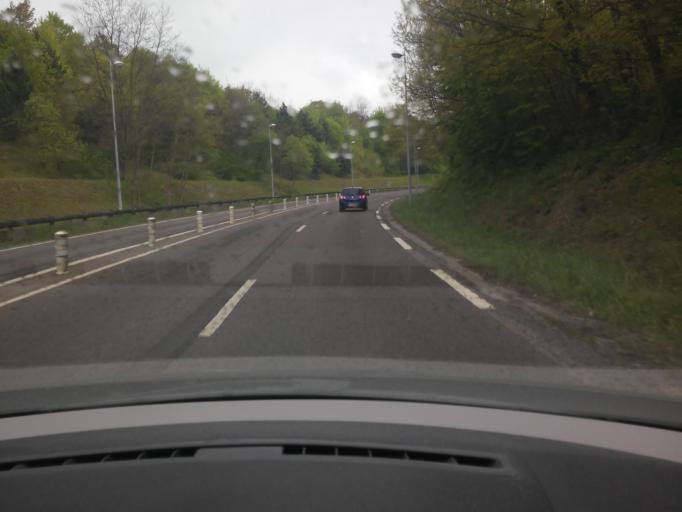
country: FR
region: Lorraine
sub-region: Departement de Meurthe-et-Moselle
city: Laxou
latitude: 48.6852
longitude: 6.1382
